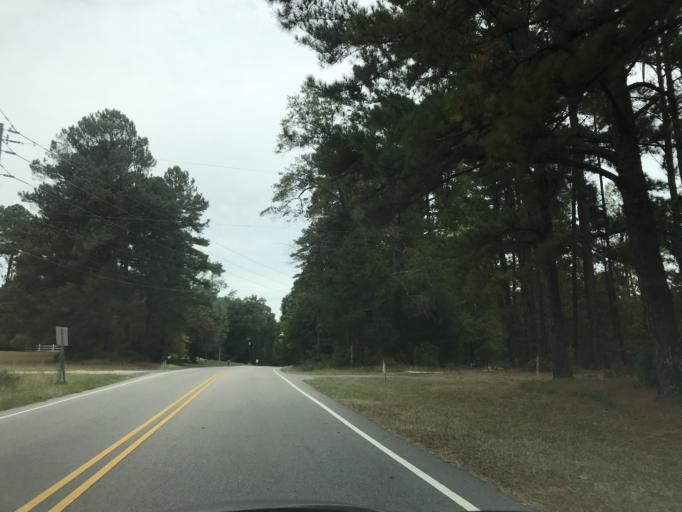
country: US
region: North Carolina
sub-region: Wake County
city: Knightdale
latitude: 35.8514
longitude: -78.5120
